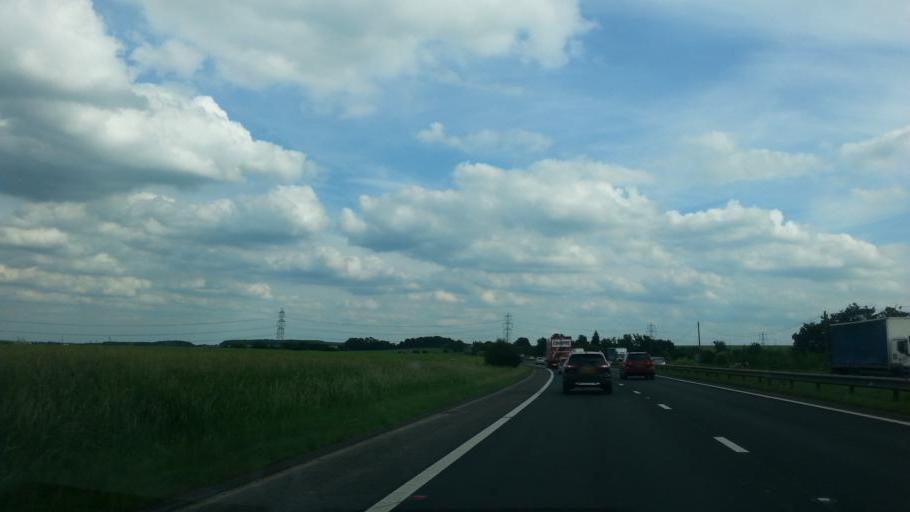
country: GB
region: England
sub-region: City and Borough of Wakefield
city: Darrington
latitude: 53.6409
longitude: -1.2535
